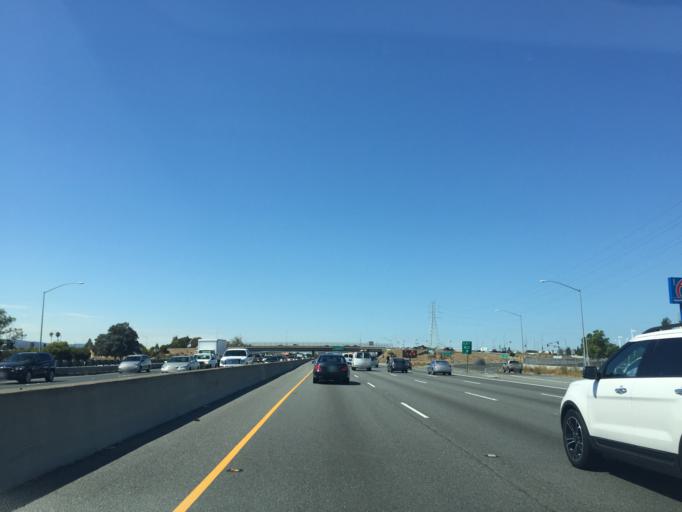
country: US
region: California
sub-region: San Mateo County
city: Belmont
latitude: 37.5240
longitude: -122.2675
